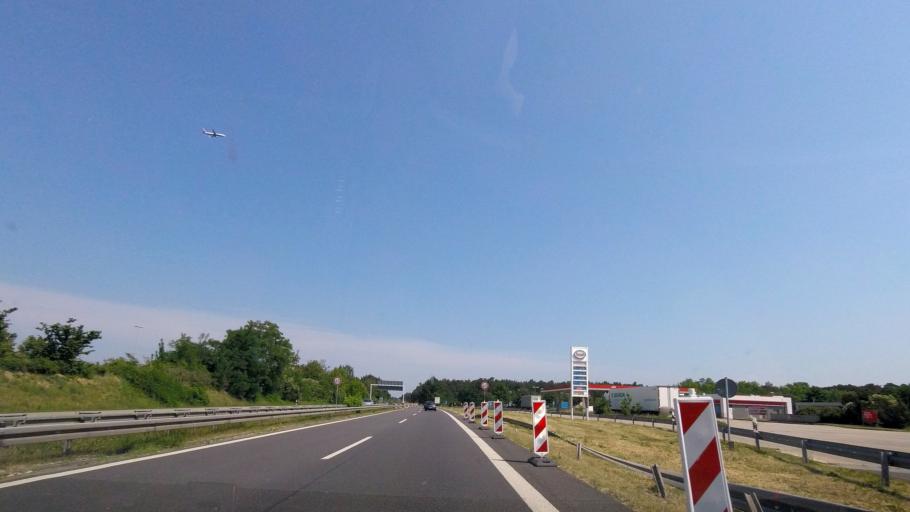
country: DE
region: Berlin
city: Bohnsdorf
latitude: 52.3766
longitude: 13.5619
